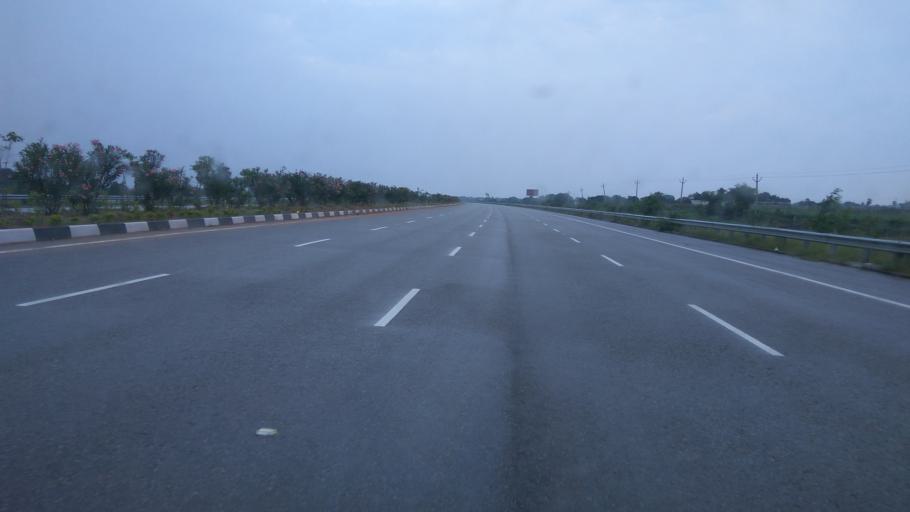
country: IN
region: Telangana
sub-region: Rangareddi
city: Ghatkesar
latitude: 17.4767
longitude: 78.6692
